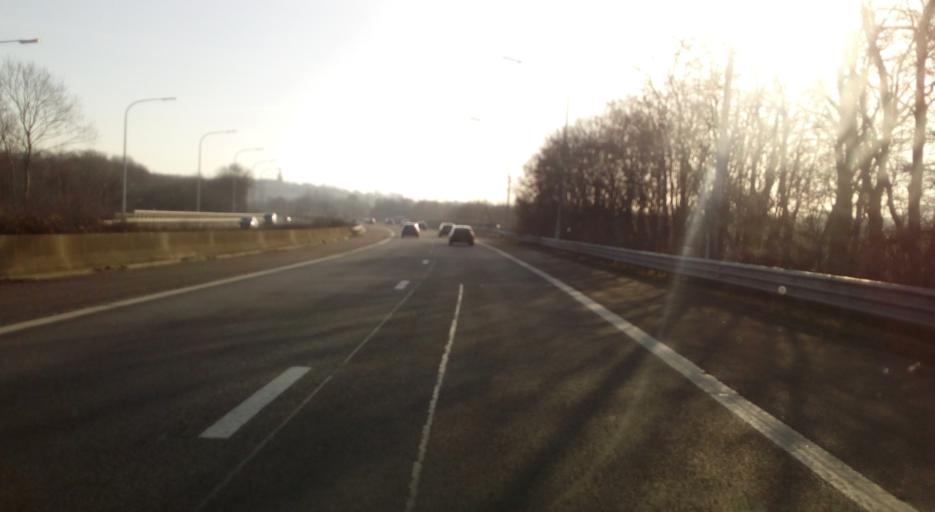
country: BE
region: Wallonia
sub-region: Province du Hainaut
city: Courcelles
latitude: 50.4645
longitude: 4.4163
